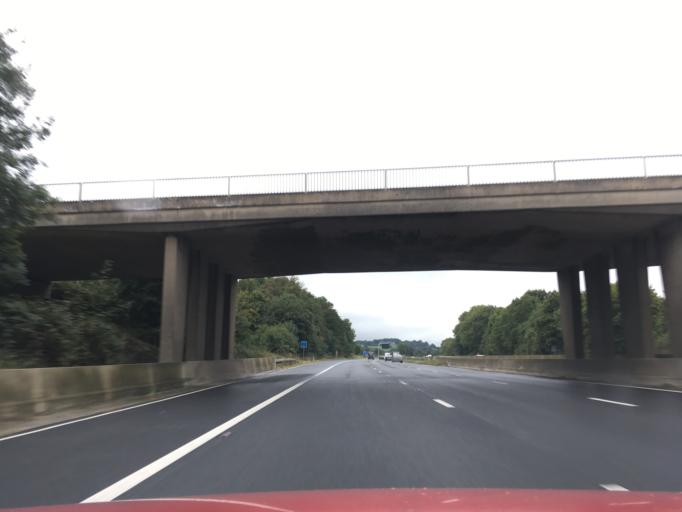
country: GB
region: England
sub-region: Gloucestershire
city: Barnwood
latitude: 51.8464
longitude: -2.1858
